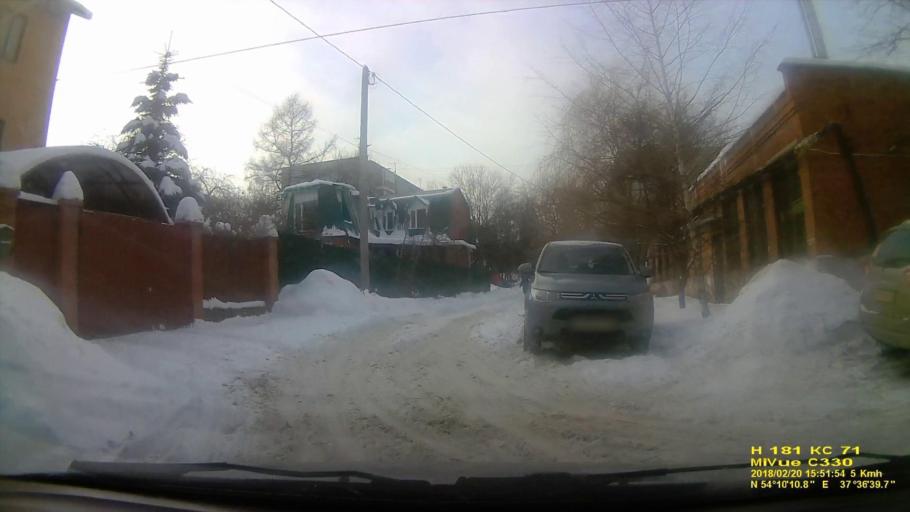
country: RU
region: Tula
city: Tula
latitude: 54.1710
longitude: 37.6138
